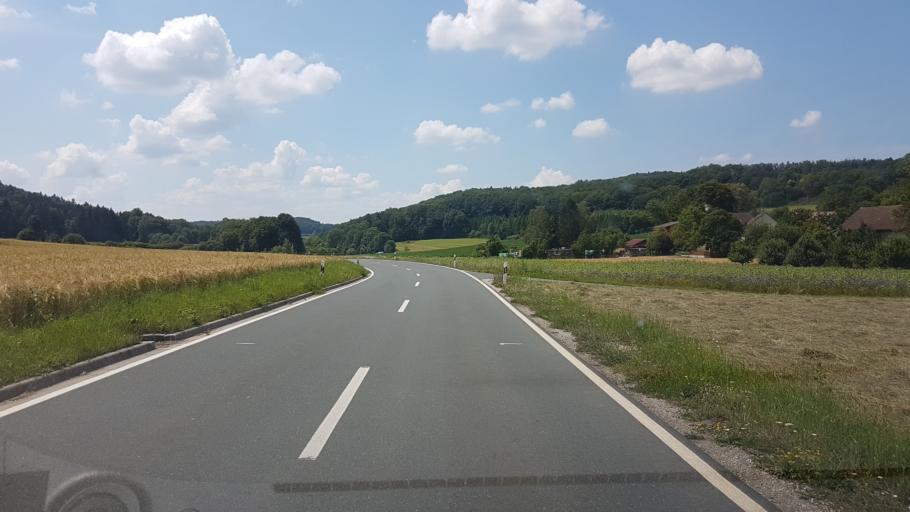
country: DE
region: Bavaria
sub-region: Upper Franconia
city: Egloffstein
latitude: 49.7528
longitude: 11.2649
